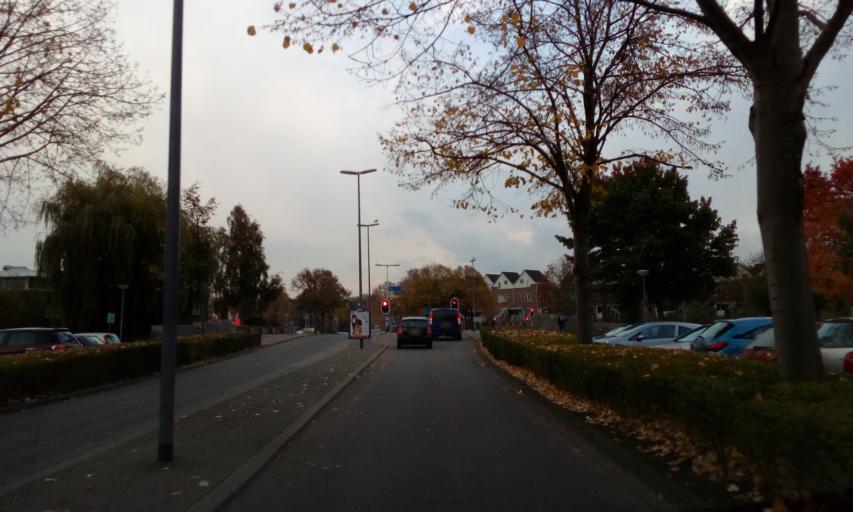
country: NL
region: South Holland
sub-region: Gemeente Capelle aan den IJssel
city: Capelle aan den IJssel
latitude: 51.9628
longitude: 4.5639
